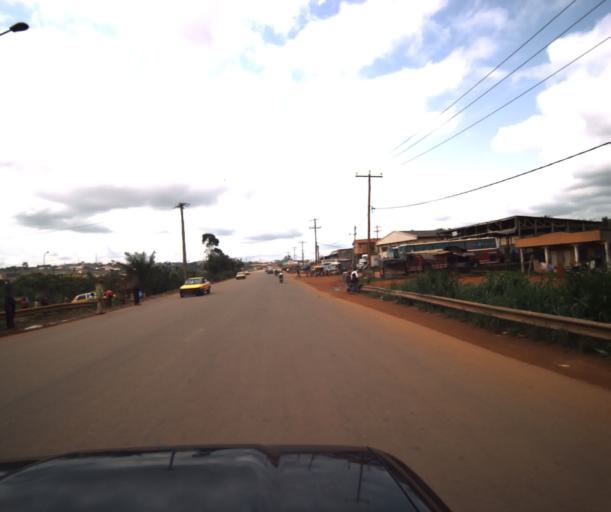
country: CM
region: Centre
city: Yaounde
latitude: 3.8093
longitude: 11.5104
